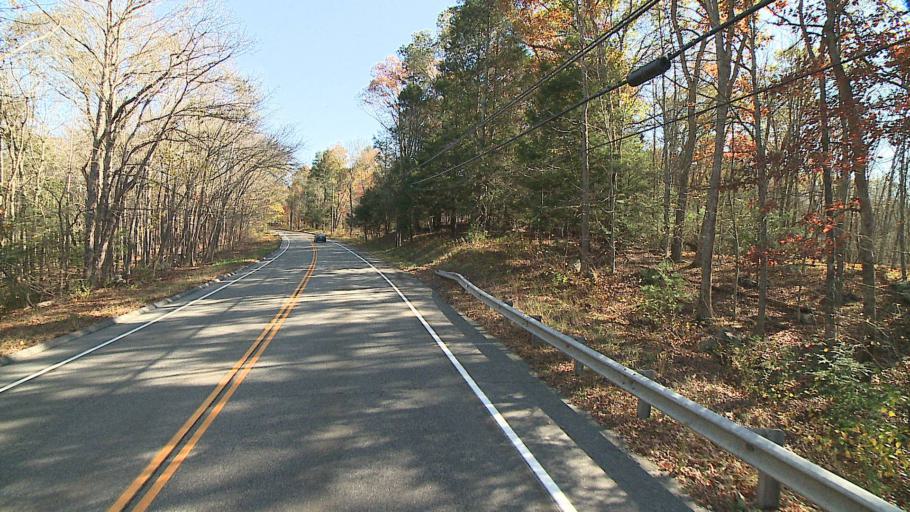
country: US
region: Connecticut
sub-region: Tolland County
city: Storrs
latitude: 41.8343
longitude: -72.2396
